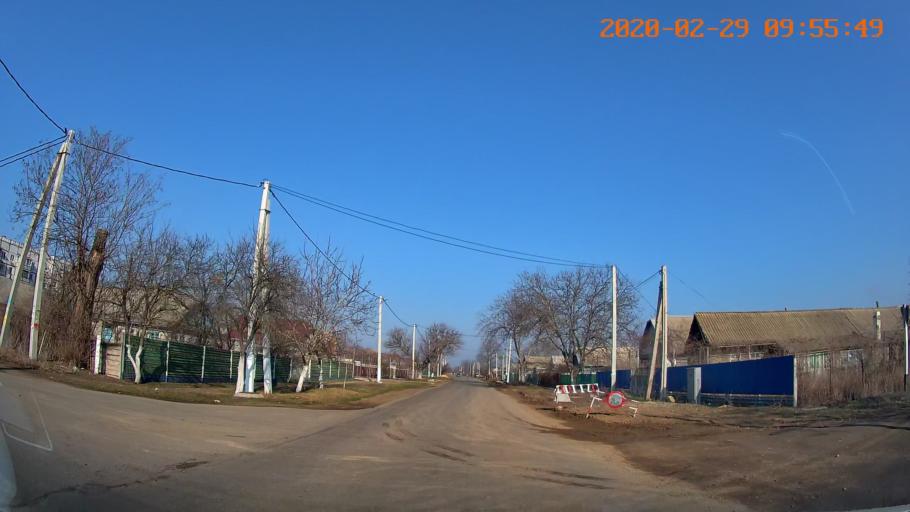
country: MD
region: Telenesti
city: Slobozia
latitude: 46.7371
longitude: 29.7082
